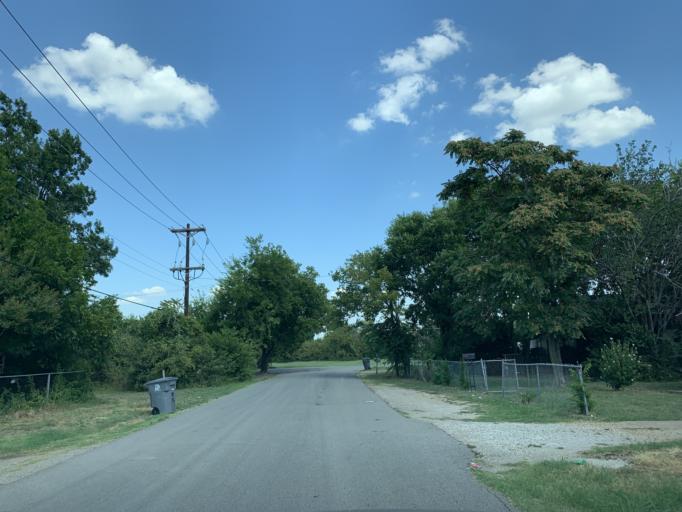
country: US
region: Texas
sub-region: Dallas County
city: DeSoto
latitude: 32.6635
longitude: -96.8186
